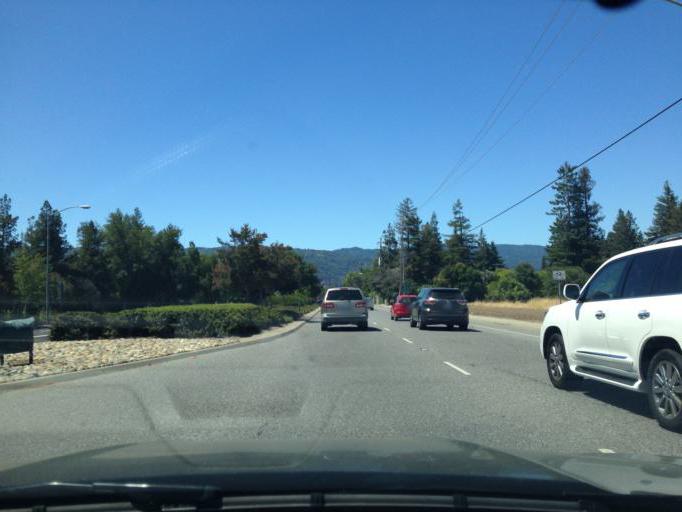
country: US
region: California
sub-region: Santa Clara County
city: Saratoga
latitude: 37.2800
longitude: -122.0043
